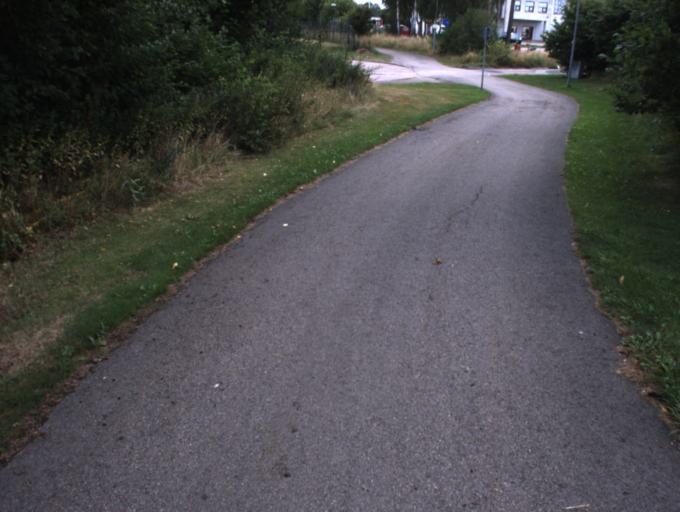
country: SE
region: Skane
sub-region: Helsingborg
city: Odakra
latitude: 56.0799
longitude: 12.7231
